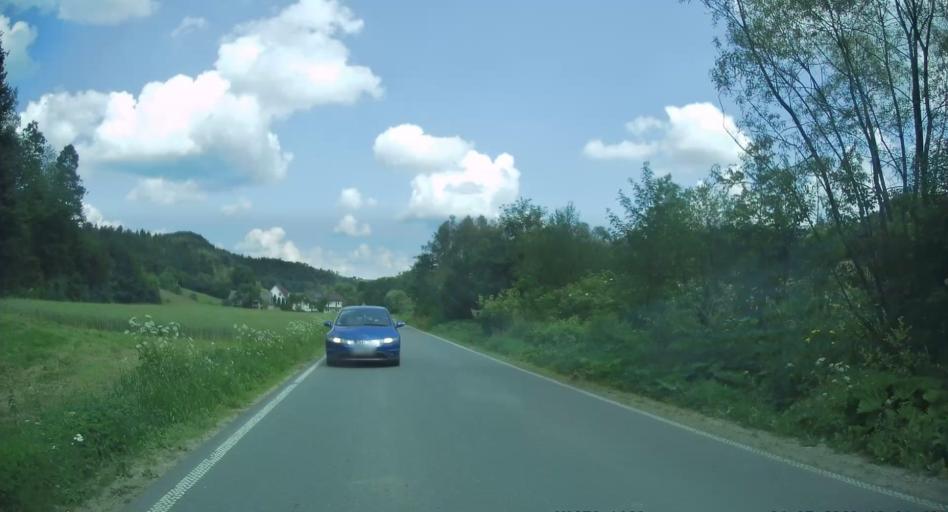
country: PL
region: Lesser Poland Voivodeship
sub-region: Powiat nowosadecki
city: Korzenna
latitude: 49.7380
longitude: 20.7709
